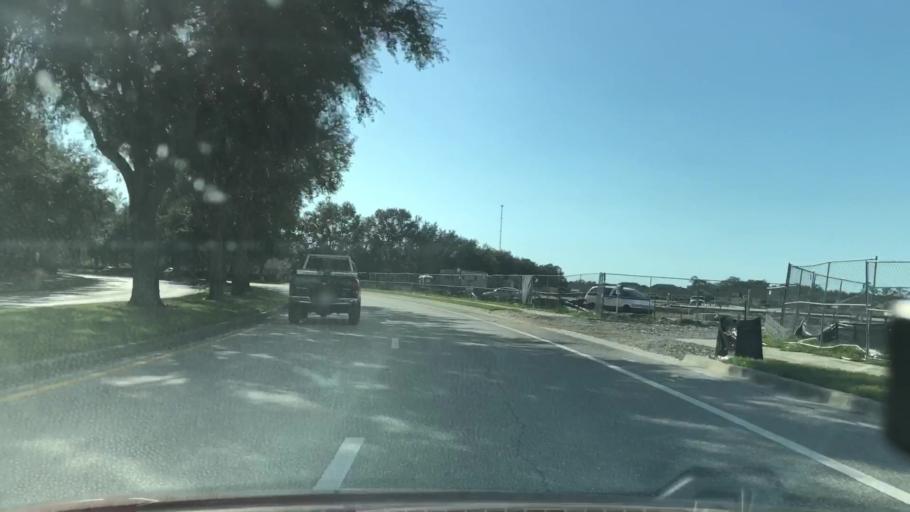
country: US
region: Florida
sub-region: Sarasota County
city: Fruitville
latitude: 27.3429
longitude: -82.4511
